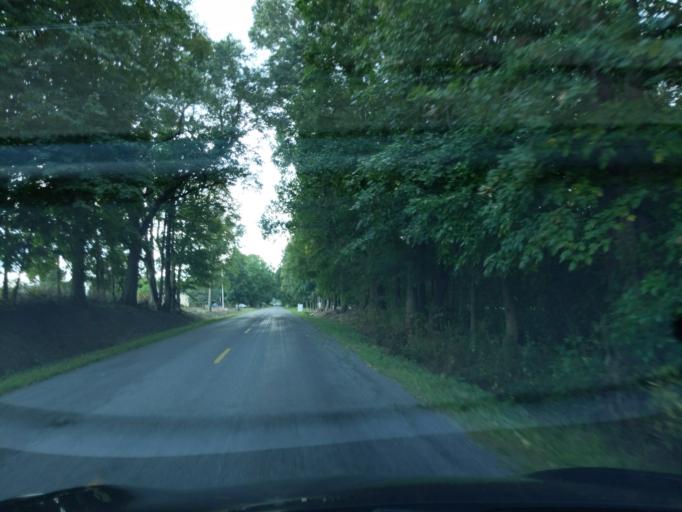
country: US
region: Michigan
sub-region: Eaton County
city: Eaton Rapids
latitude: 42.4342
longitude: -84.5803
